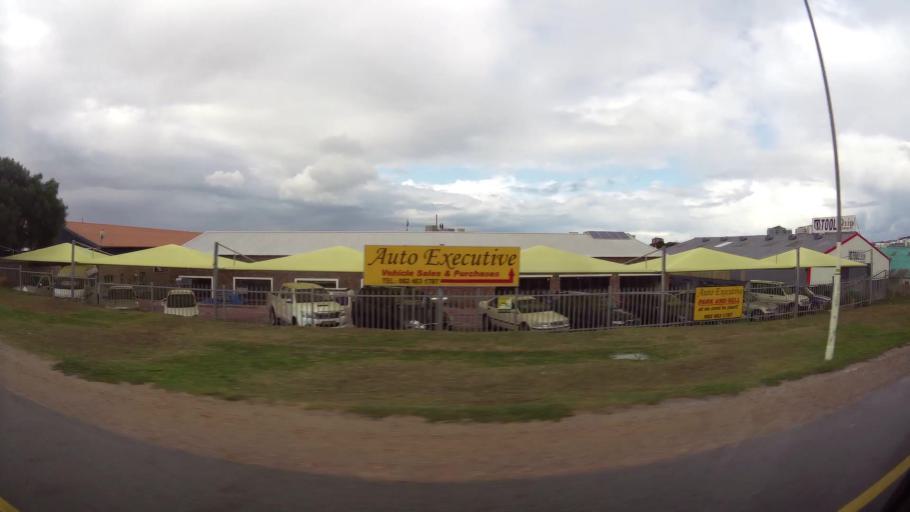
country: ZA
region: Western Cape
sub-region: Eden District Municipality
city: Mossel Bay
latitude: -34.1546
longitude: 22.1020
